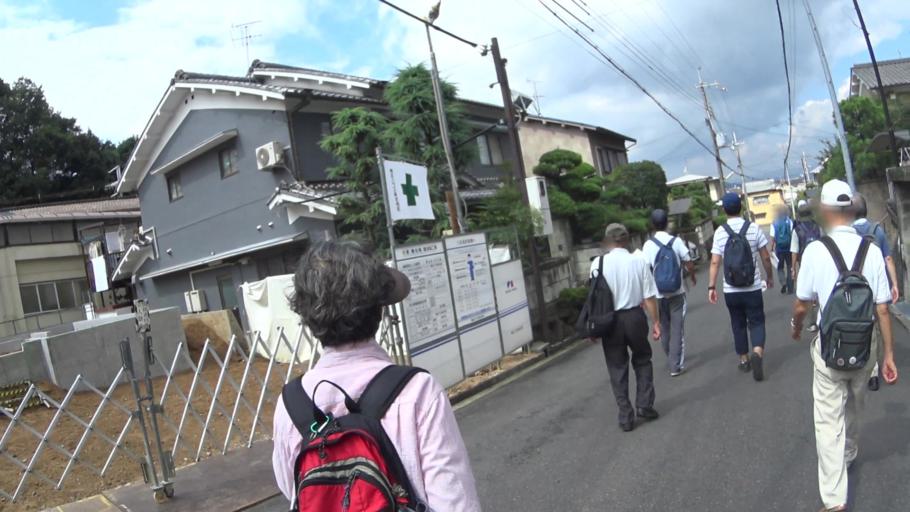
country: JP
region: Nara
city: Sakurai
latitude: 34.5043
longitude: 135.8438
